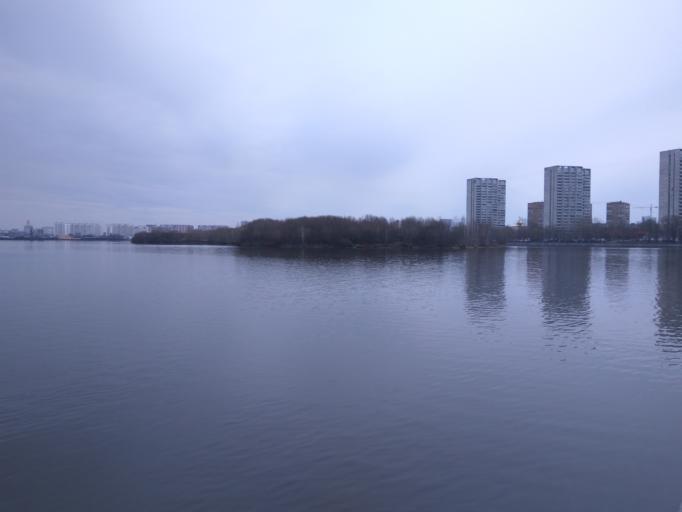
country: RU
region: Moskovskaya
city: Kozhukhovo
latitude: 55.6941
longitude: 37.6861
